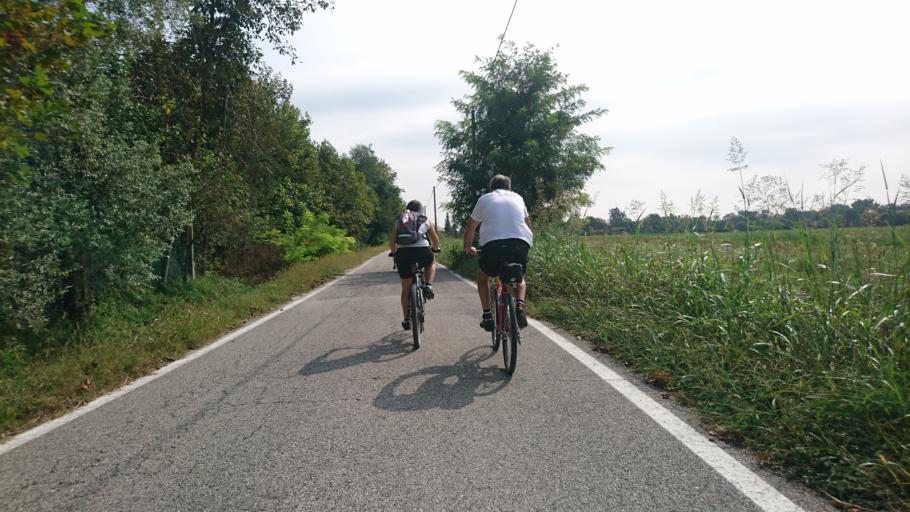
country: IT
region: Veneto
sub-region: Provincia di Padova
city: San Giorgio in Bosco
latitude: 45.5760
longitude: 11.7704
